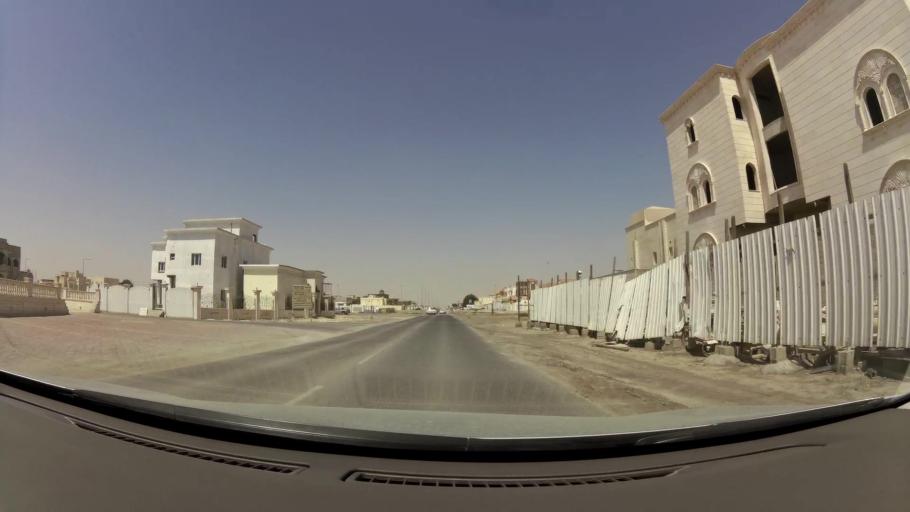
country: QA
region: Baladiyat ar Rayyan
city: Ar Rayyan
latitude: 25.2472
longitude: 51.4024
